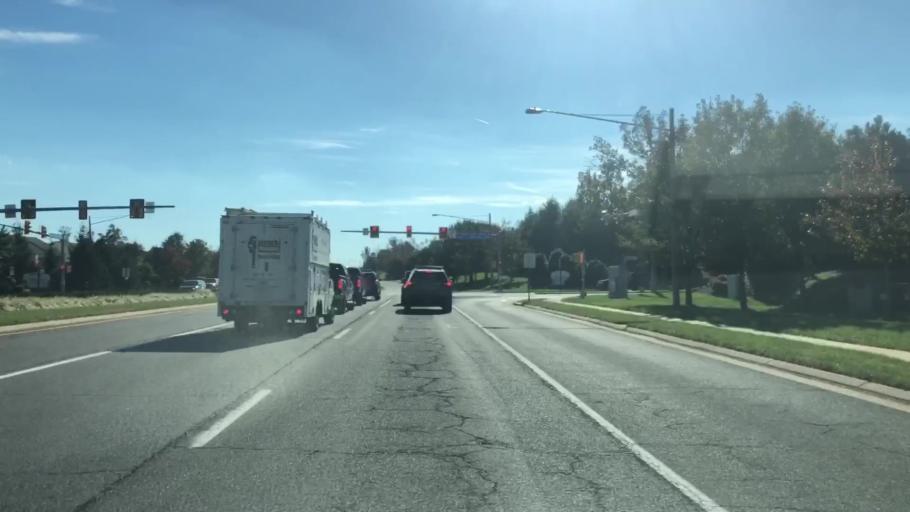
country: US
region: Virginia
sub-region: Prince William County
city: Linton Hall
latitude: 38.7420
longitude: -77.5772
